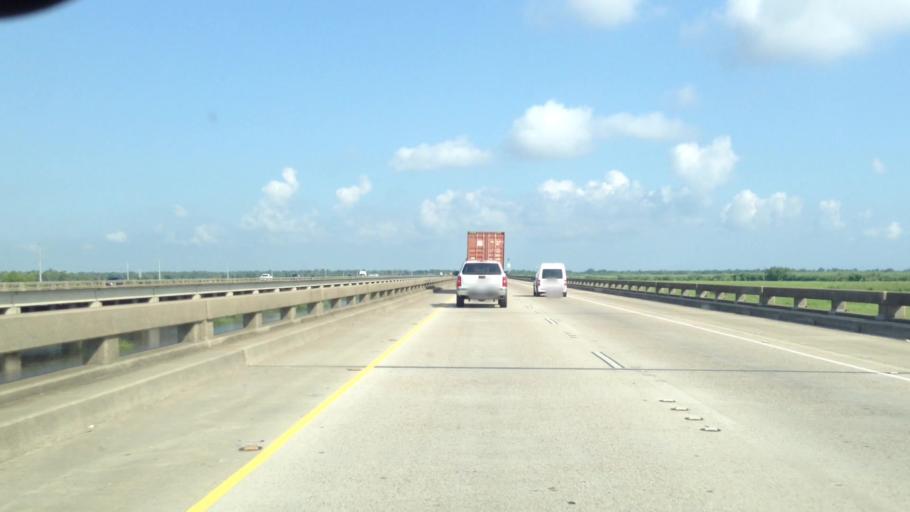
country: US
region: Louisiana
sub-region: Saint Charles Parish
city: New Sarpy
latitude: 30.0402
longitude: -90.3487
